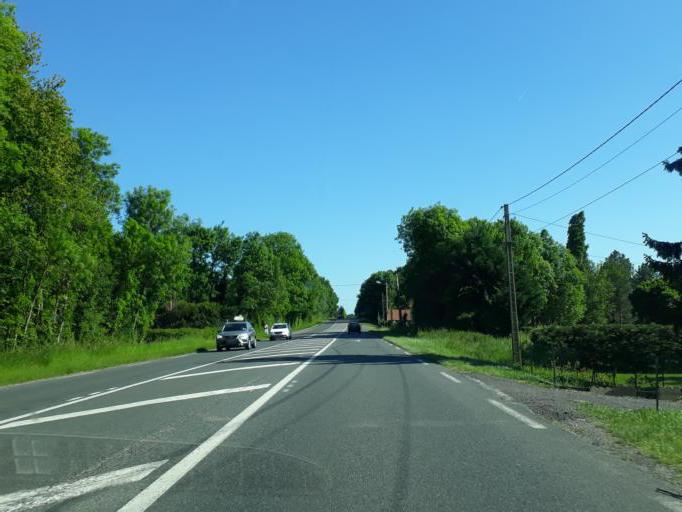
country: FR
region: Centre
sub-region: Departement du Cher
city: Lere
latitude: 47.4802
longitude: 2.9254
